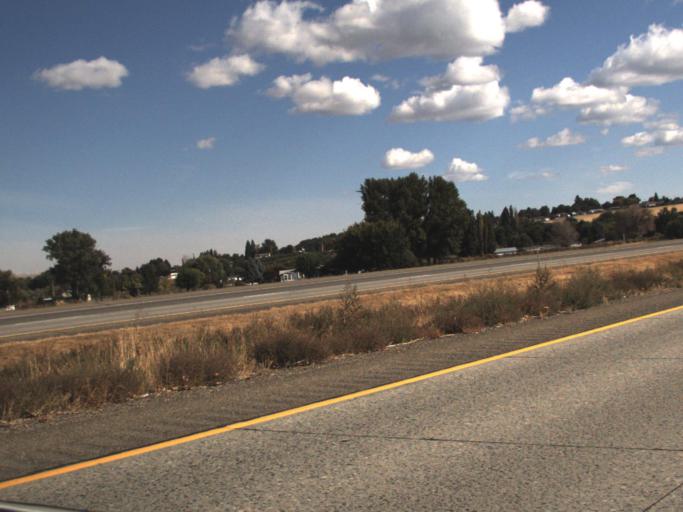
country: US
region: Washington
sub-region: Yakima County
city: Sunnyside
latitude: 46.3194
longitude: -120.0590
